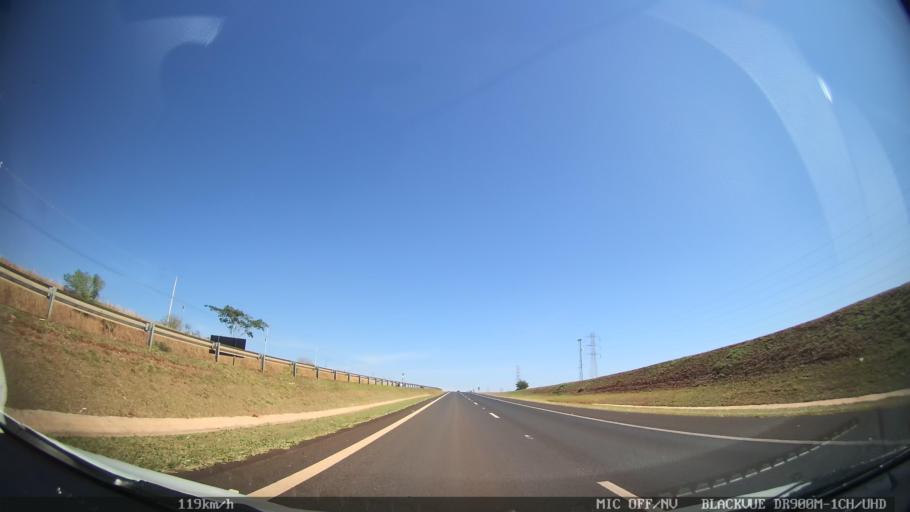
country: BR
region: Sao Paulo
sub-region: Ribeirao Preto
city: Ribeirao Preto
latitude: -21.1438
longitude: -47.8735
